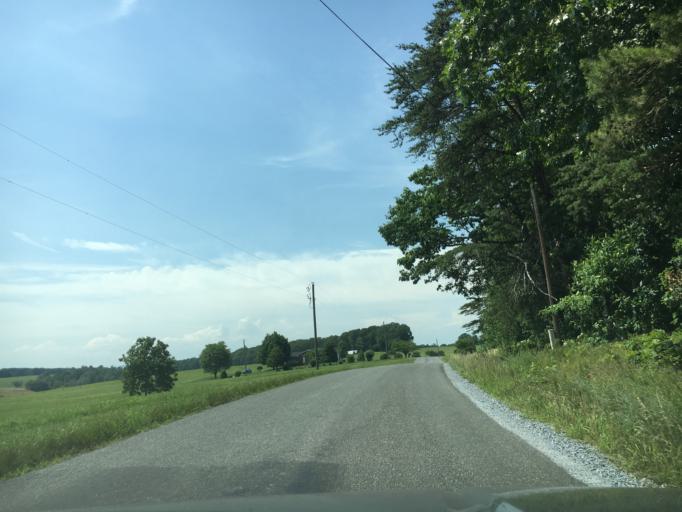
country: US
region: Virginia
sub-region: Pittsylvania County
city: Gretna
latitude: 36.9120
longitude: -79.4202
